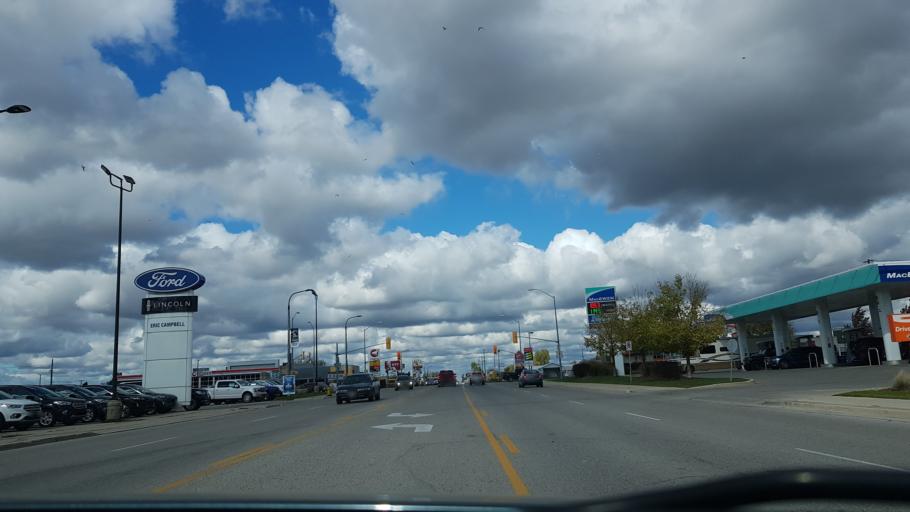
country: CA
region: Ontario
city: South Huron
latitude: 43.3608
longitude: -81.4835
